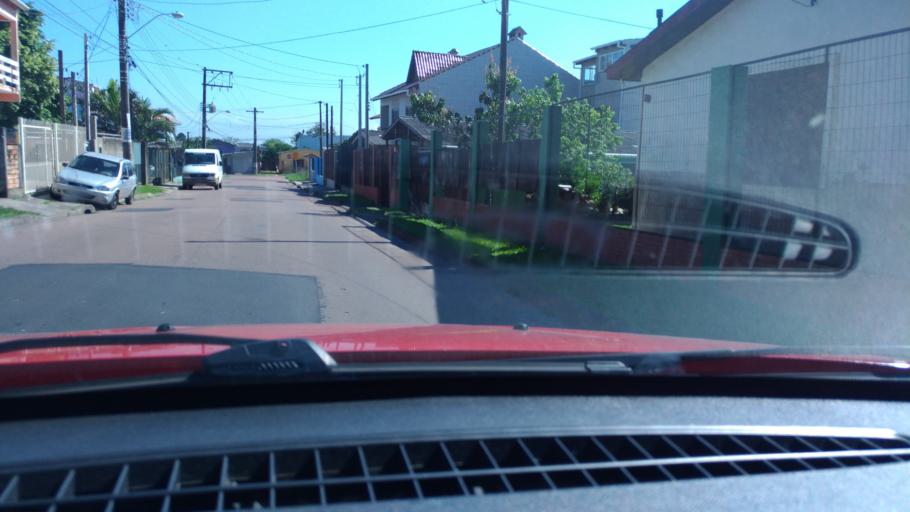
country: BR
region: Rio Grande do Sul
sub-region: Cachoeirinha
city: Cachoeirinha
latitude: -30.0358
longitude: -51.1273
